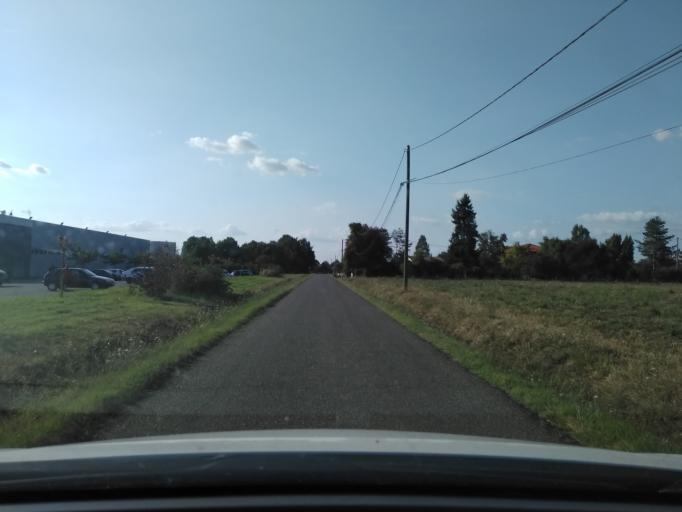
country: FR
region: Midi-Pyrenees
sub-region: Departement du Tarn-et-Garonne
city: Montech
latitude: 43.9650
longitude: 1.2471
